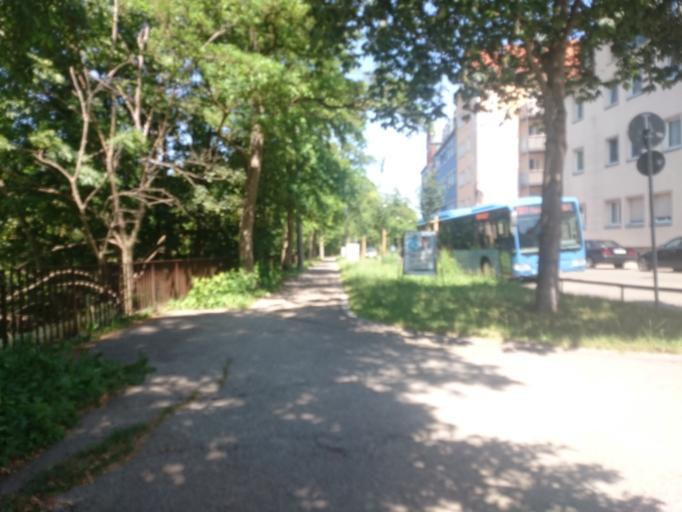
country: DE
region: Bavaria
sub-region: Swabia
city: Augsburg
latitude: 48.3747
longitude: 10.8877
